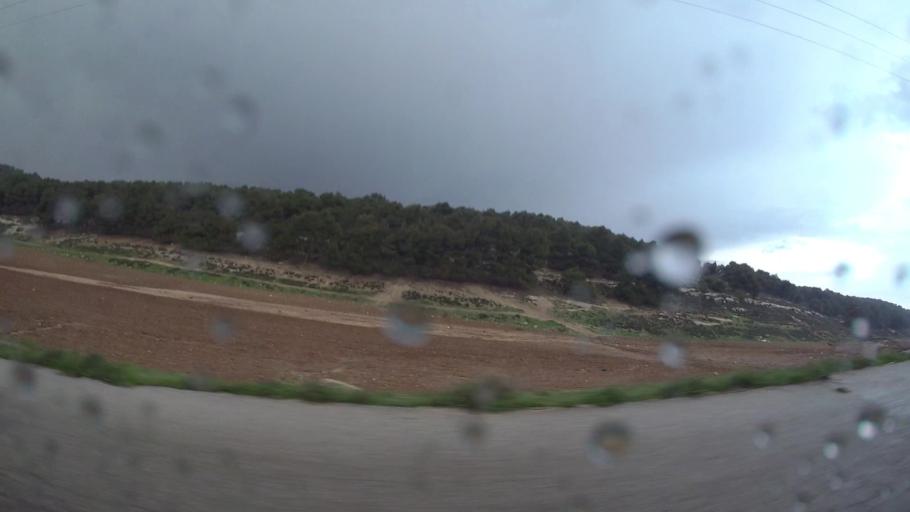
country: JO
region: Amman
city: Umm as Summaq
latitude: 31.8633
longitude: 35.8702
